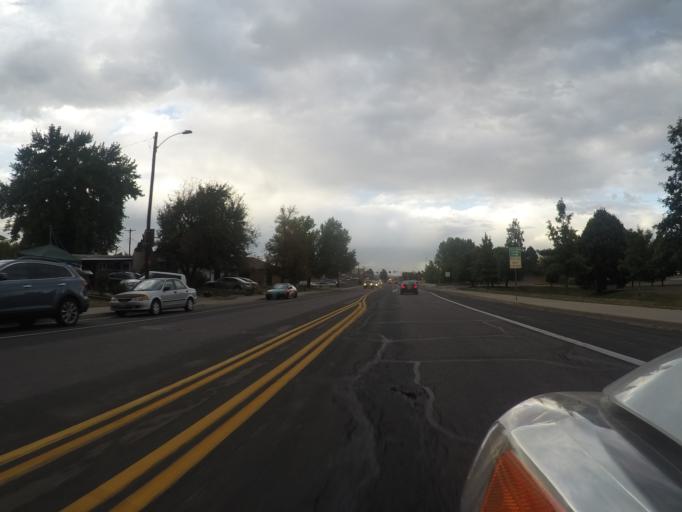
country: US
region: Colorado
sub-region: Arapahoe County
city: Littleton
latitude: 39.6221
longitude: -105.0068
